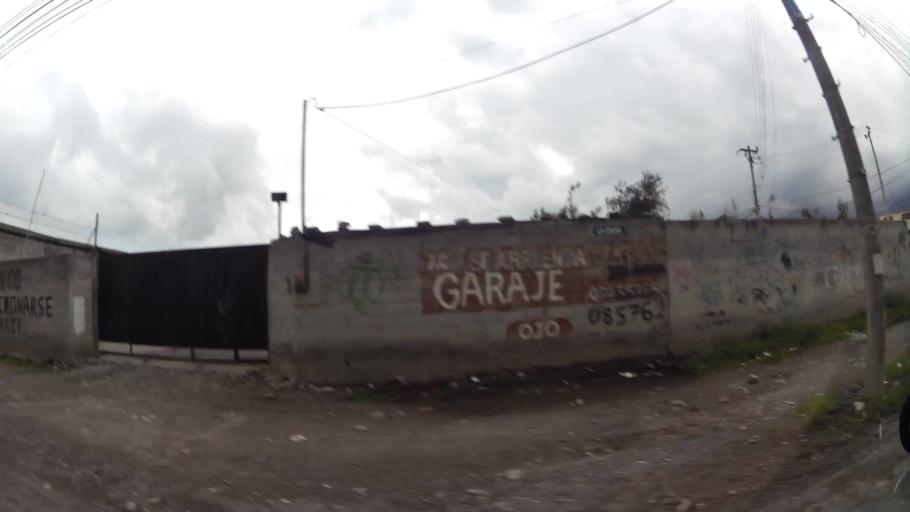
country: EC
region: Pichincha
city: Quito
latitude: -0.3123
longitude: -78.5425
